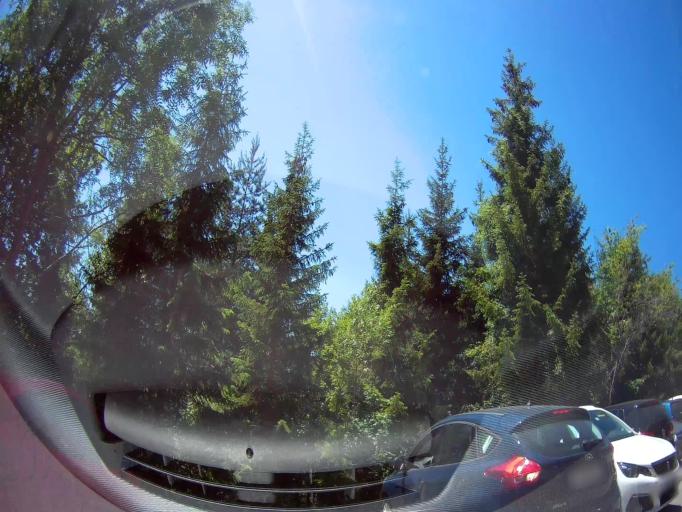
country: AT
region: Salzburg
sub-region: Politischer Bezirk Sankt Johann im Pongau
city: Werfen
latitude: 47.4965
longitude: 13.1943
